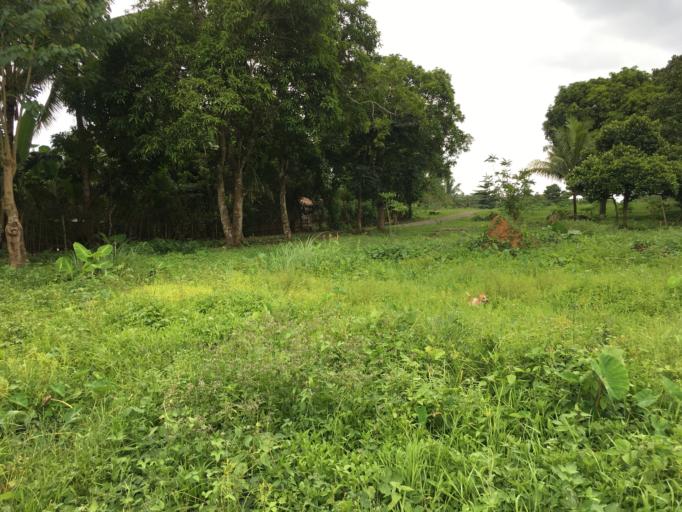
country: PH
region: Western Visayas
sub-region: Province of Aklan
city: Banga
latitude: 11.6244
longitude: 122.3451
